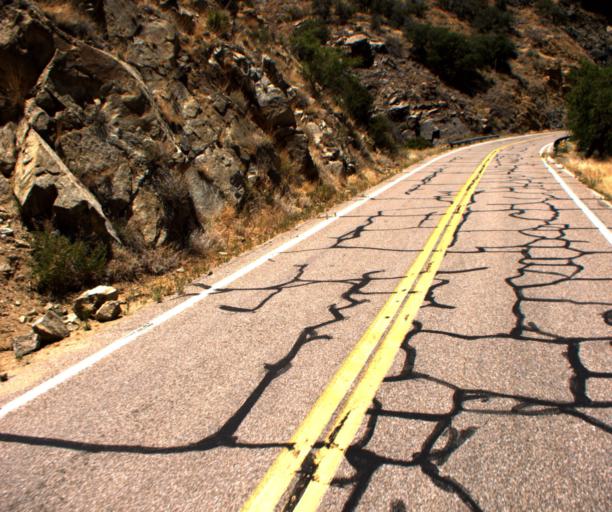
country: US
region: Arizona
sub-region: Pima County
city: Sells
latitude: 31.9701
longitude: -111.6132
